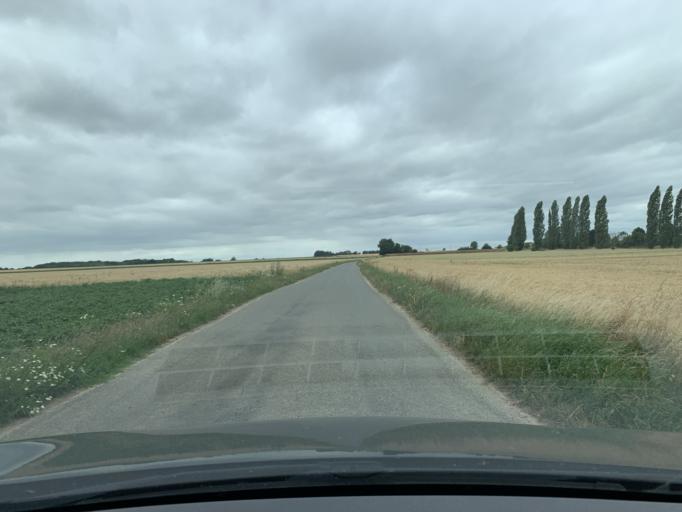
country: FR
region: Nord-Pas-de-Calais
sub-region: Departement du Pas-de-Calais
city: Oisy-le-Verger
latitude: 50.2149
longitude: 3.1349
